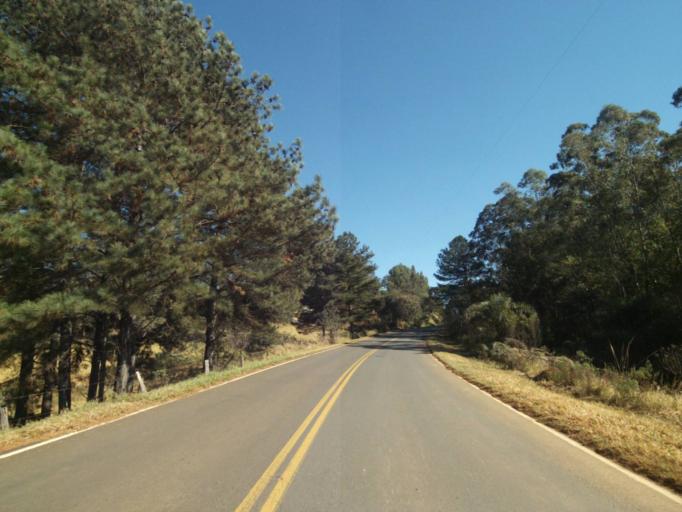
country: BR
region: Parana
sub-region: Tibagi
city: Tibagi
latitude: -24.5010
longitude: -50.4479
